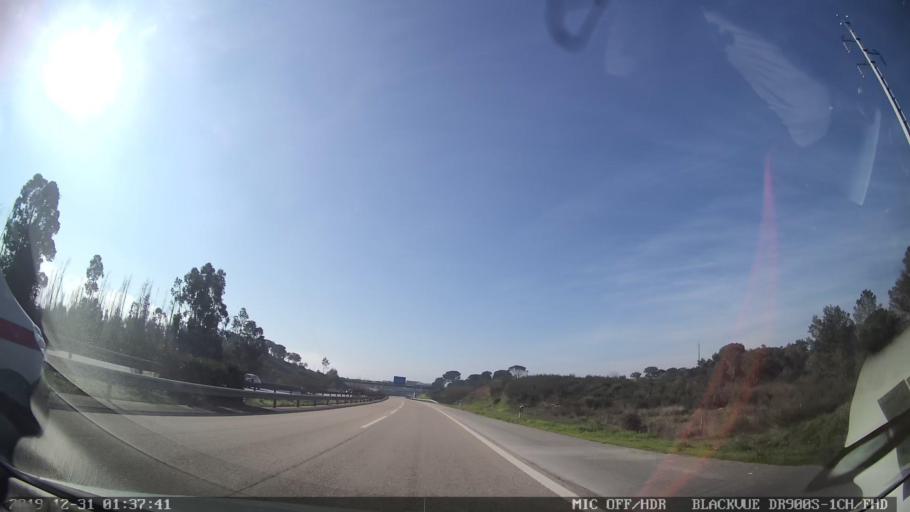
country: PT
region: Santarem
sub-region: Constancia
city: Constancia
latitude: 39.4872
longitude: -8.3211
